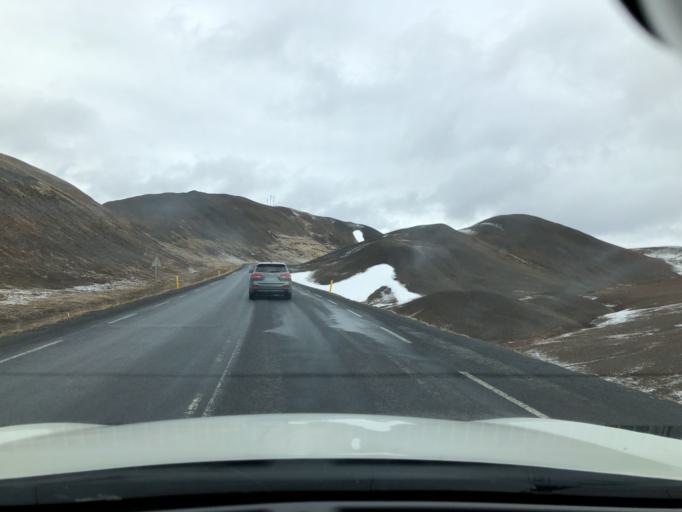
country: IS
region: Northeast
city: Laugar
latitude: 65.6434
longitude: -16.8312
